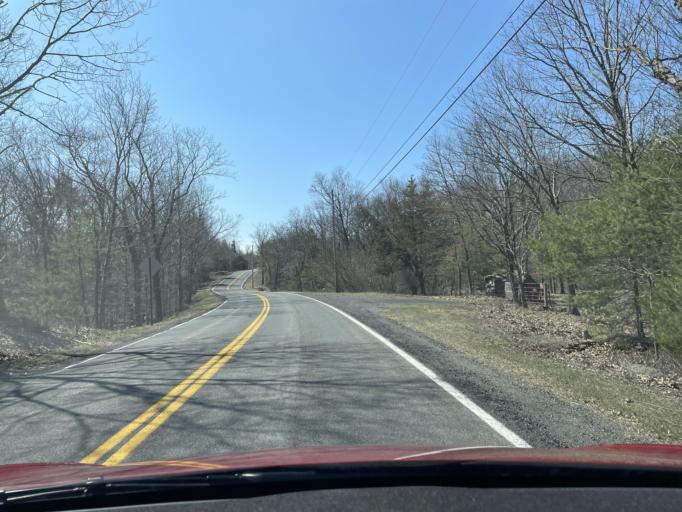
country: US
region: New York
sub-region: Ulster County
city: Zena
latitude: 42.0812
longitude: -74.0645
